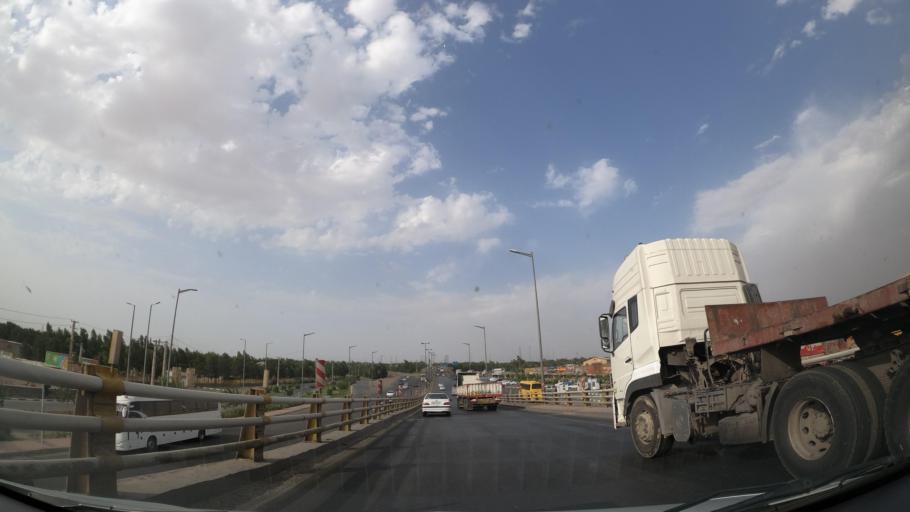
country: IR
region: Qom
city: Qom
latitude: 34.6769
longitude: 50.8929
